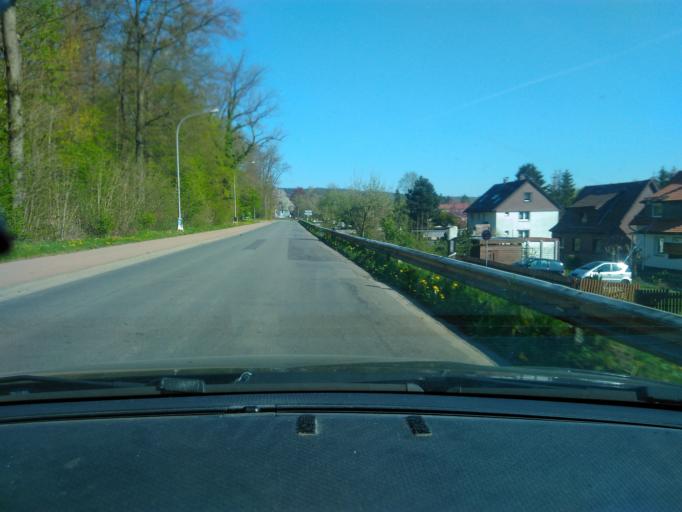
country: DE
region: Lower Saxony
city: Osterode am Harz
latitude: 51.7204
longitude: 10.2680
